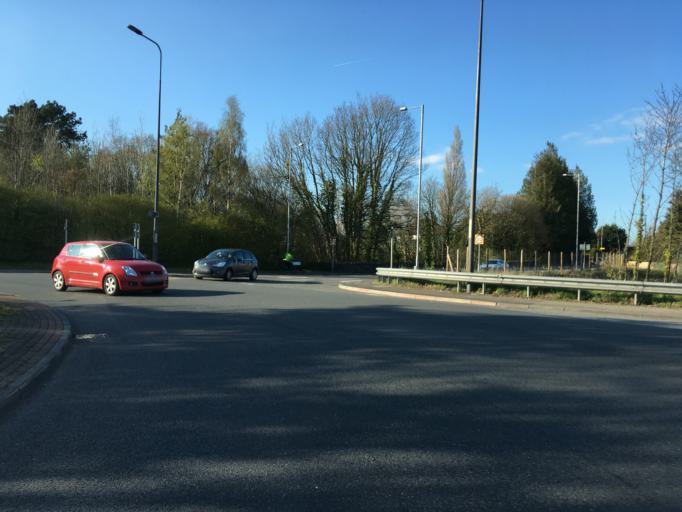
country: GB
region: Wales
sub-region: Torfaen County Borough
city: Cwmbran
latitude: 51.6218
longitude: -3.0100
